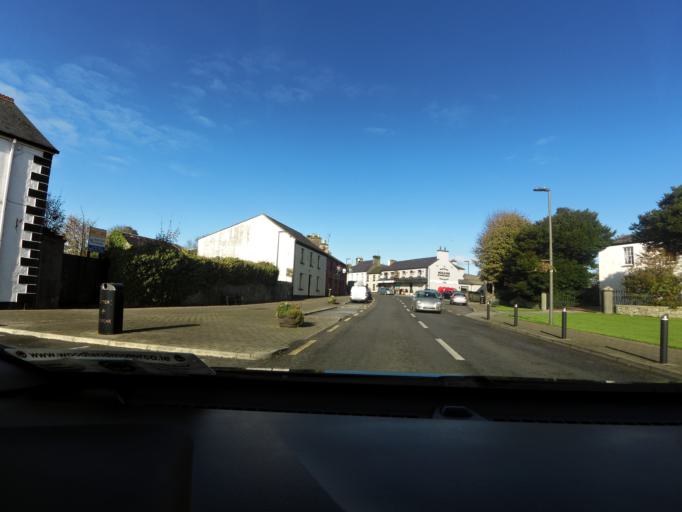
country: IE
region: Connaught
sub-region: Maigh Eo
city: Ballinrobe
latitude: 53.5193
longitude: -9.0866
